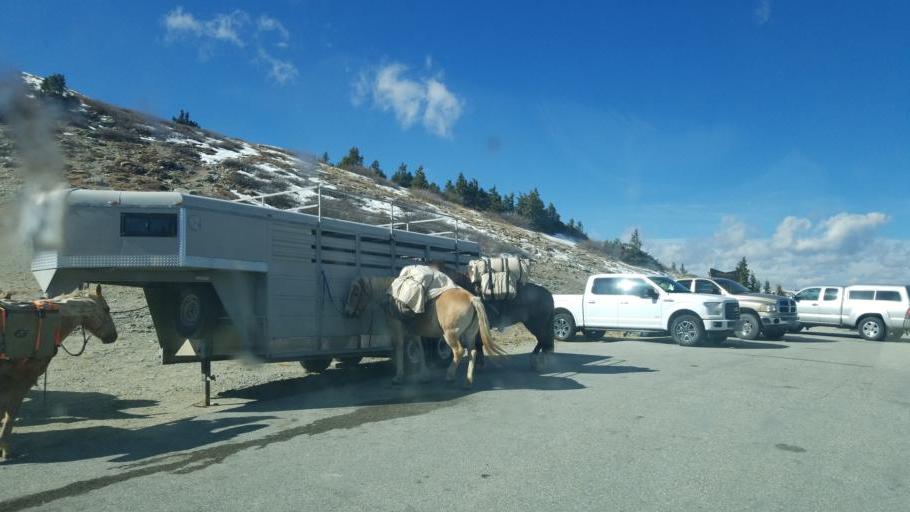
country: US
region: Colorado
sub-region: Chaffee County
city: Buena Vista
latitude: 38.8277
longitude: -106.4092
